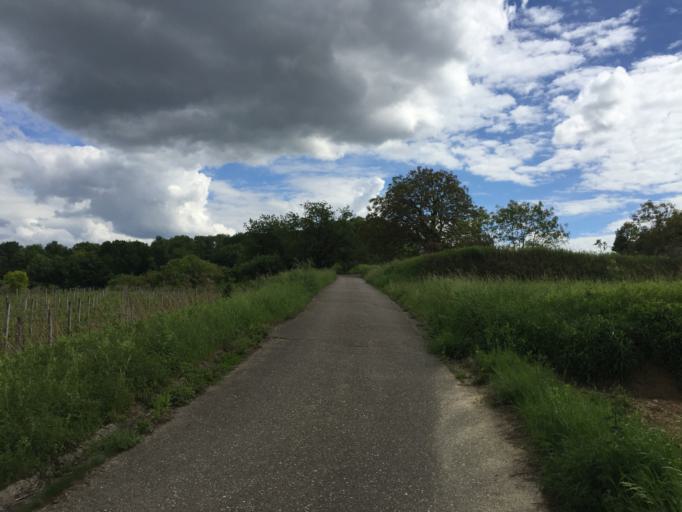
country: DE
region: Baden-Wuerttemberg
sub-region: Freiburg Region
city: Malterdingen
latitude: 48.1567
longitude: 7.8108
